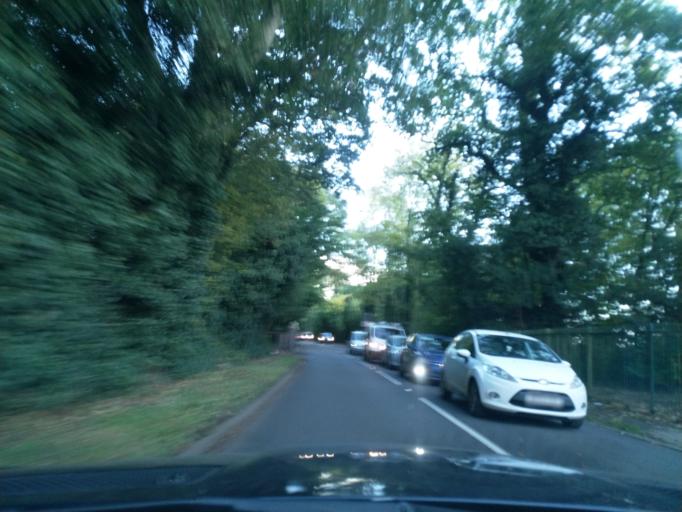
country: GB
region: England
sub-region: Solihull
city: Cheswick Green
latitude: 52.3503
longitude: -1.7760
